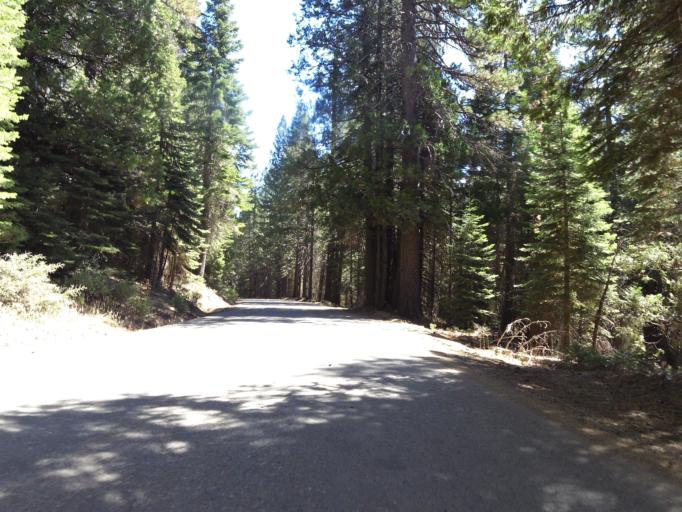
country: US
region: California
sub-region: Madera County
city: Oakhurst
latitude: 37.4210
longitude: -119.5586
